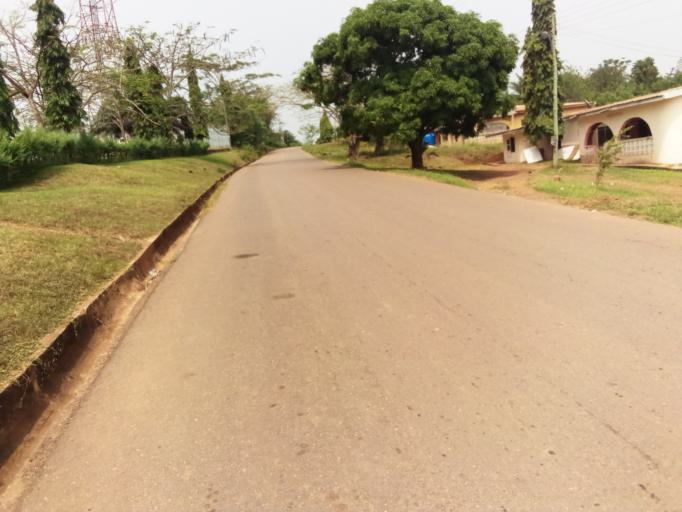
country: CI
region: Sud-Comoe
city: Ayame
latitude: 5.8301
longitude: -2.8204
